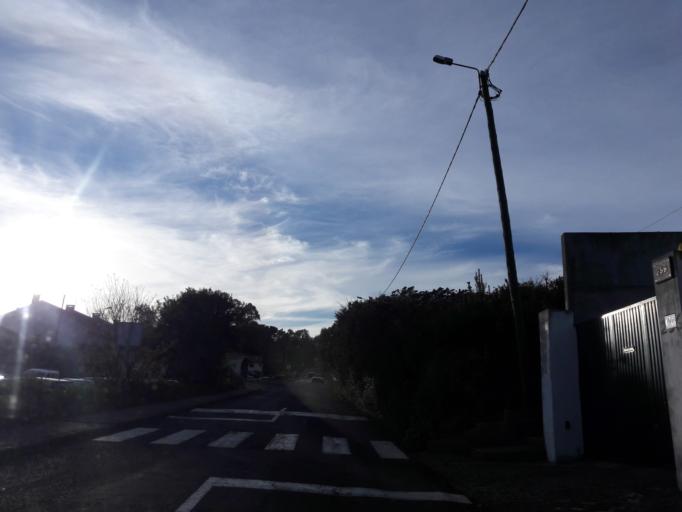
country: PT
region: Madeira
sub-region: Santa Cruz
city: Camacha
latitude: 32.6712
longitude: -16.8471
